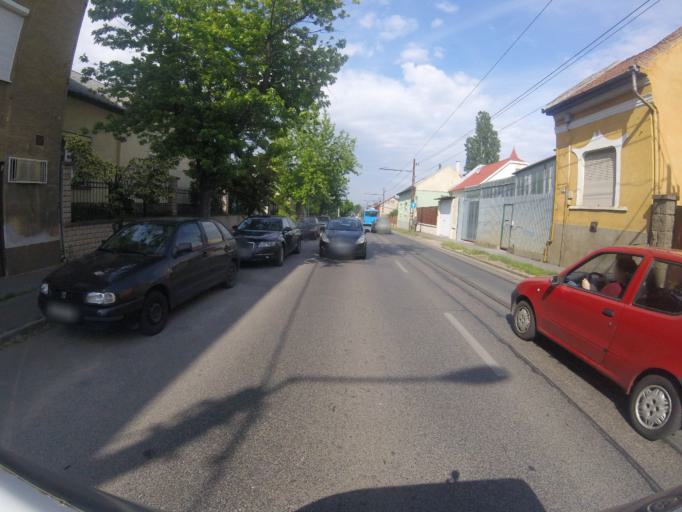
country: HU
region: Budapest
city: Budapest XX. keruelet
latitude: 47.4381
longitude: 19.1144
